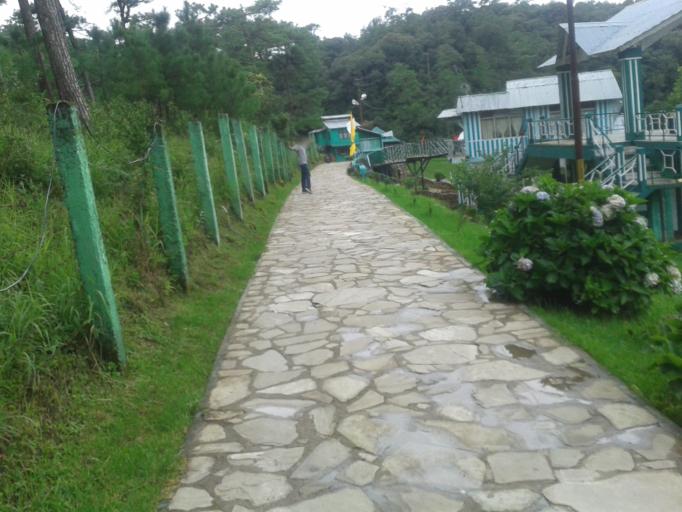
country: IN
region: Meghalaya
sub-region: East Khasi Hills
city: Shillong
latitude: 25.5396
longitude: 91.8218
